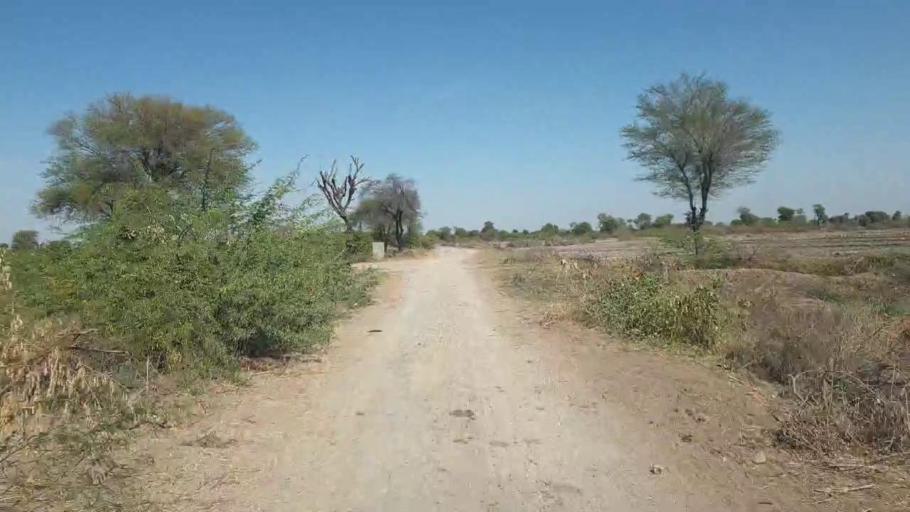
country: PK
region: Sindh
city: Dhoro Naro
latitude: 25.4244
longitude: 69.6200
